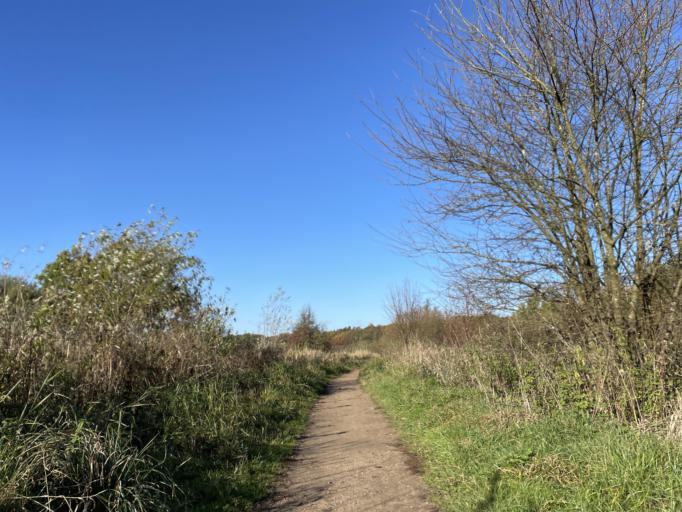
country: DE
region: Lower Saxony
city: Deutsch Evern
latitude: 53.2213
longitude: 10.4223
